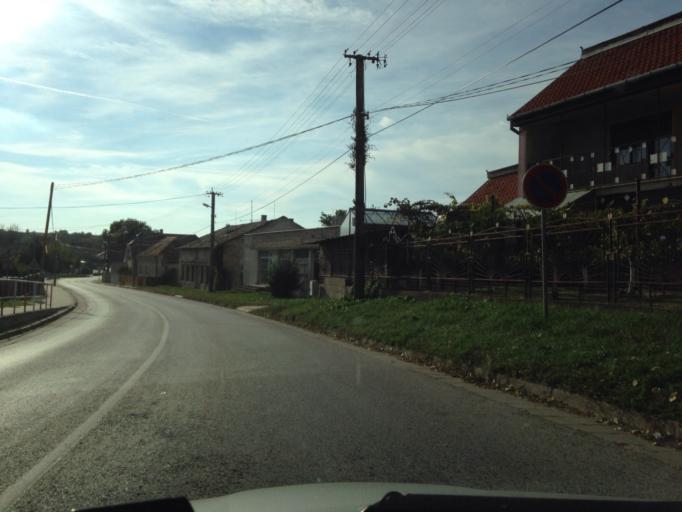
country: SK
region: Nitriansky
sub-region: Okres Komarno
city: Hurbanovo
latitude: 47.8704
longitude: 18.2747
